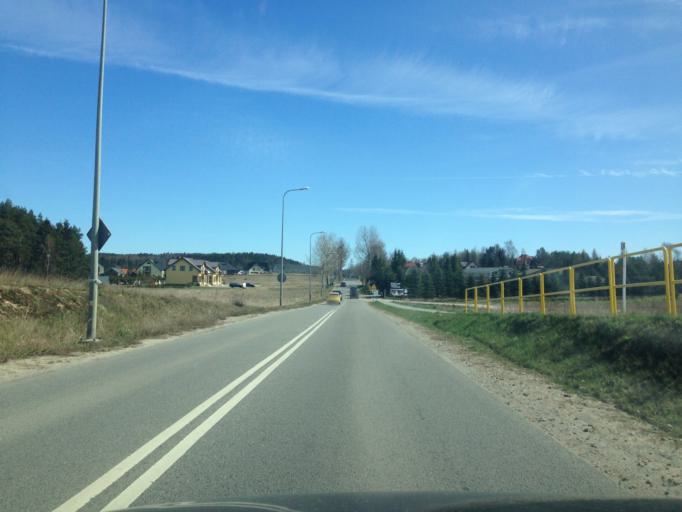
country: PL
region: Pomeranian Voivodeship
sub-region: Powiat kartuski
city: Chwaszczyno
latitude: 54.4872
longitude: 18.4299
